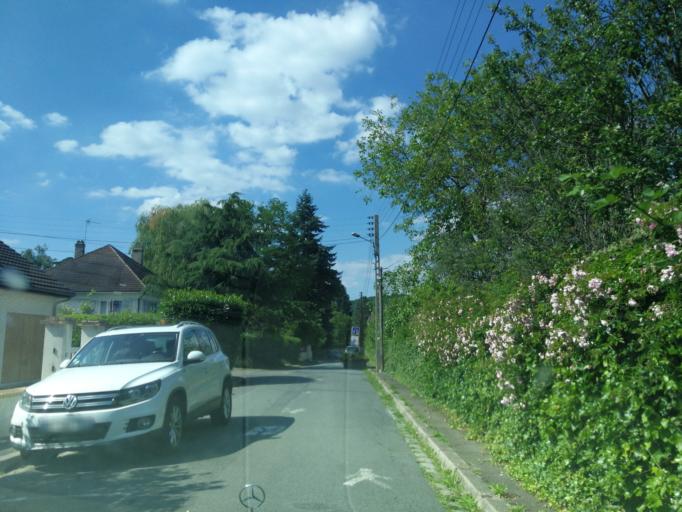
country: FR
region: Ile-de-France
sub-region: Departement des Yvelines
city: Saint-Remy-les-Chevreuse
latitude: 48.7151
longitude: 2.0656
